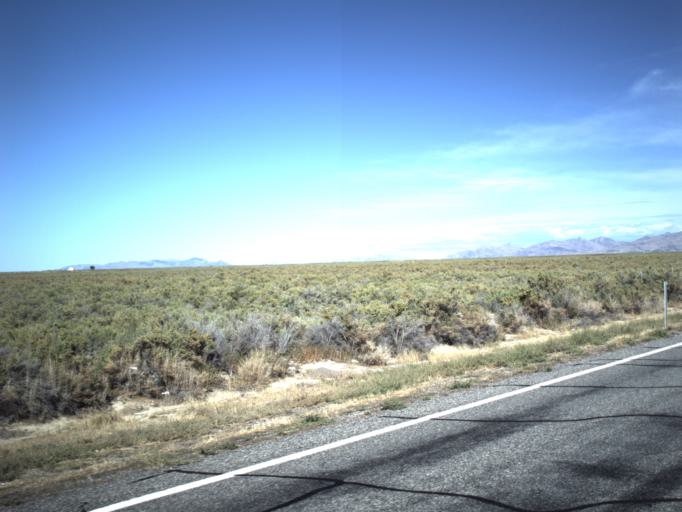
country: US
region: Utah
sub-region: Millard County
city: Delta
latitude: 39.3530
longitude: -112.5236
